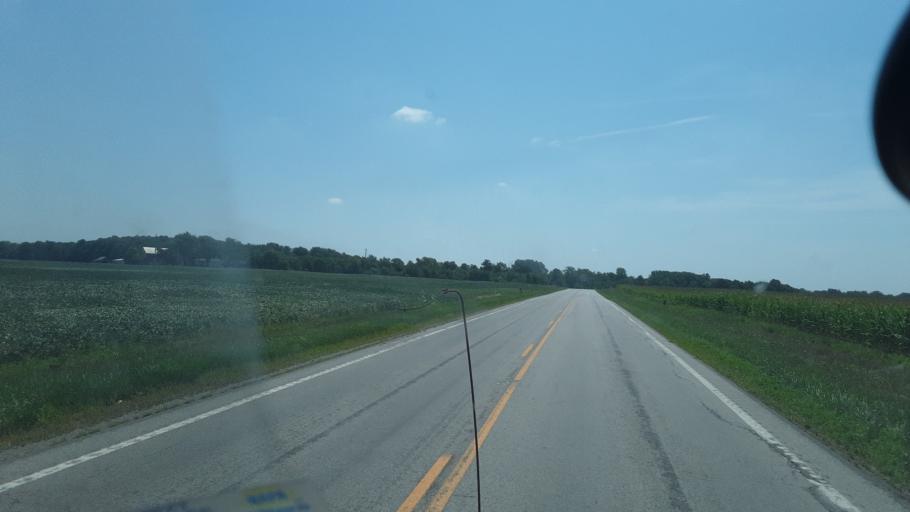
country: US
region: Ohio
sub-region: Hancock County
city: Arlington
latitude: 40.9299
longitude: -83.5635
